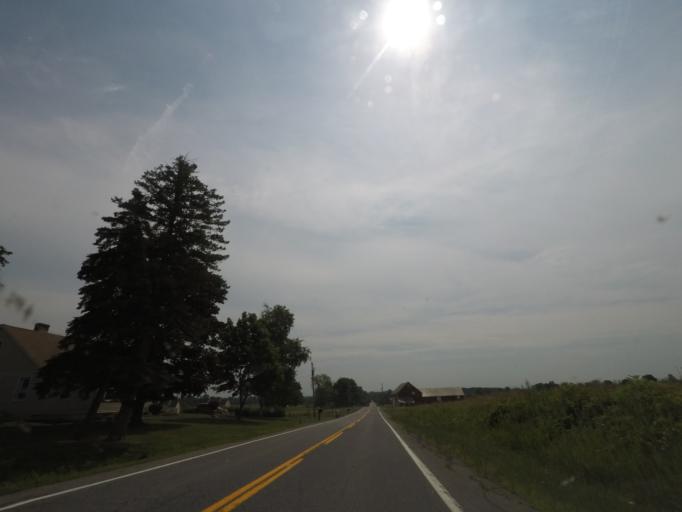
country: US
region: New York
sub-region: Saratoga County
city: Mechanicville
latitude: 42.8881
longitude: -73.7096
